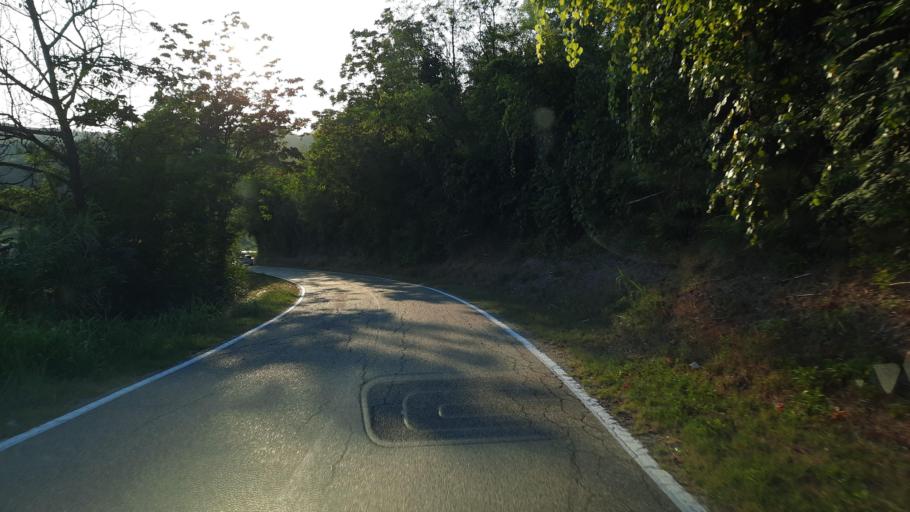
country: IT
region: Piedmont
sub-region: Provincia di Alessandria
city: Cereseto
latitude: 45.0846
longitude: 8.3142
